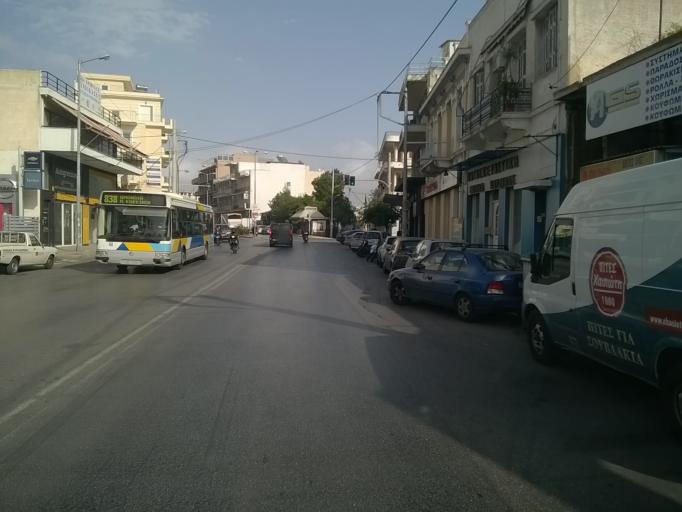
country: GR
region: Attica
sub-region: Nomos Piraios
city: Nikaia
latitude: 37.9612
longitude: 23.6565
